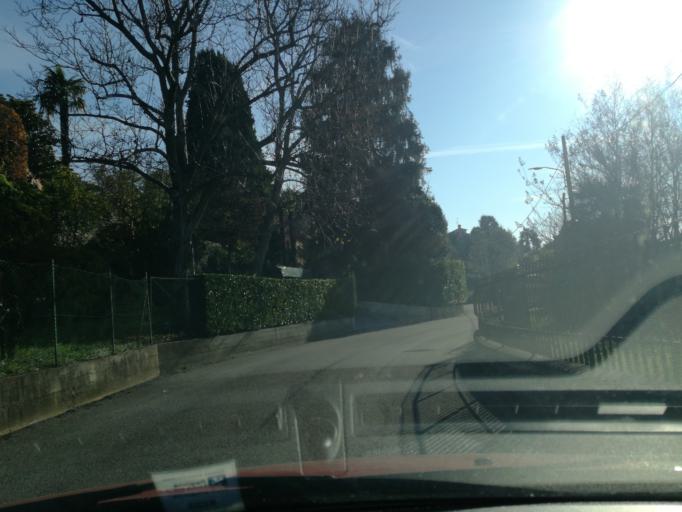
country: IT
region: Lombardy
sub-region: Provincia di Lecco
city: Robbiate
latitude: 45.7006
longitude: 9.4314
